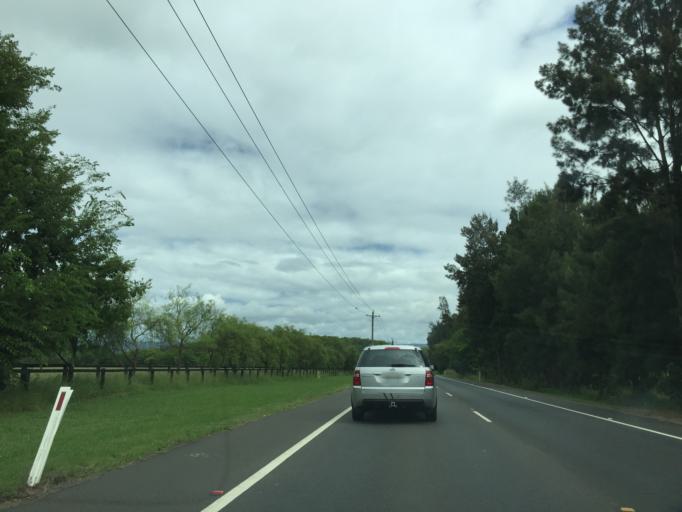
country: AU
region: New South Wales
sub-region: Hawkesbury
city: Richmond
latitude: -33.5925
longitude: 150.7377
